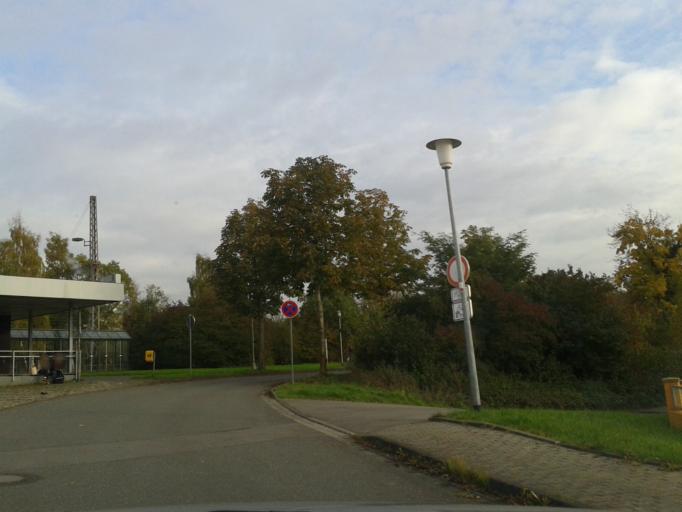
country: DE
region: North Rhine-Westphalia
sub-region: Regierungsbezirk Detmold
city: Horn-Bad Meinberg
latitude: 51.8816
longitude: 8.9542
